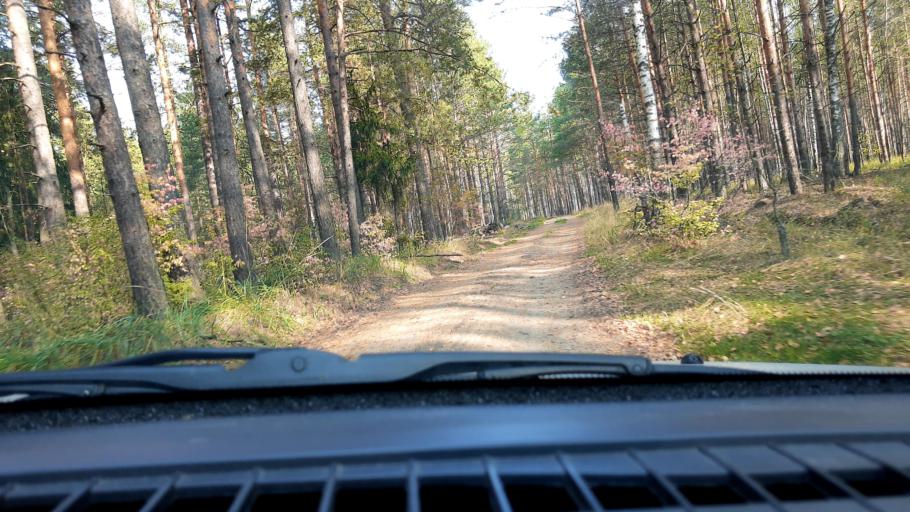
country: RU
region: Nizjnij Novgorod
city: Lukino
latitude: 56.3901
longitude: 43.6278
